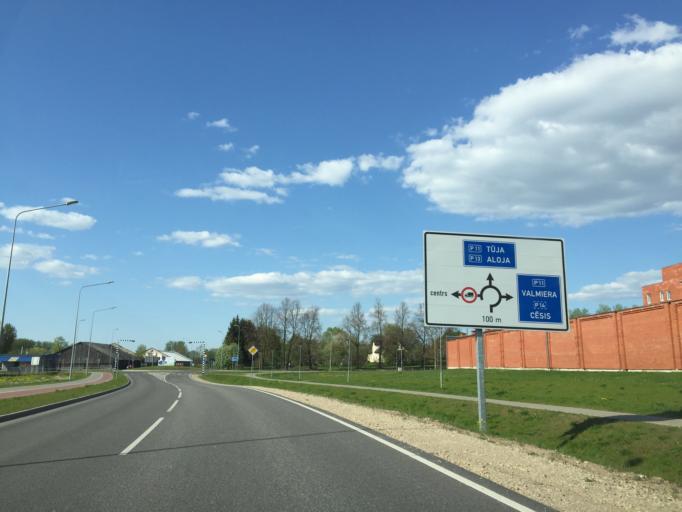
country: LV
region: Limbazu Rajons
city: Limbazi
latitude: 57.5117
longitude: 24.7239
